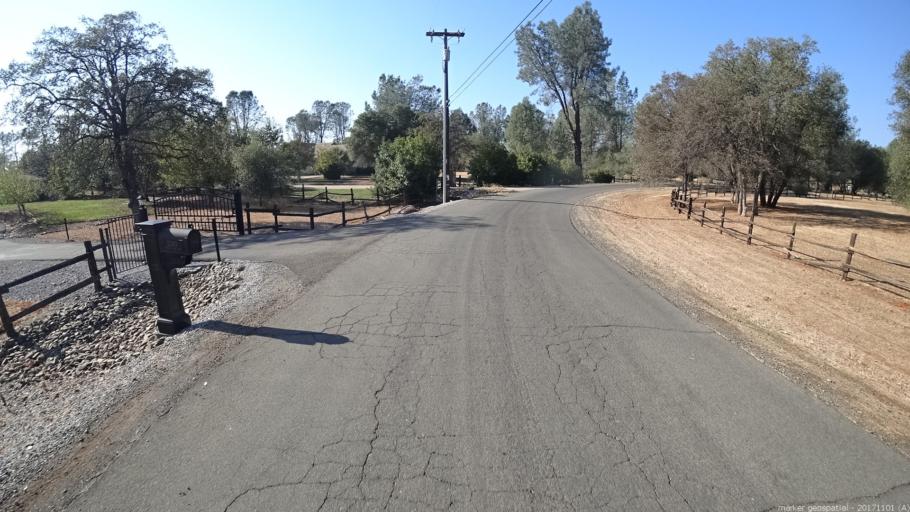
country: US
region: California
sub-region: Shasta County
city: Shasta Lake
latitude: 40.6741
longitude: -122.3438
